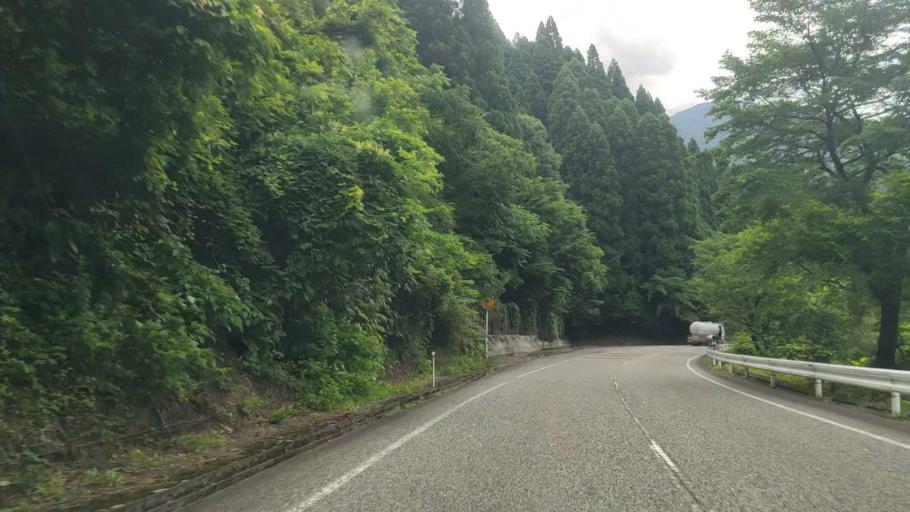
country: JP
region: Tottori
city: Yonago
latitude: 35.2519
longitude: 133.4400
